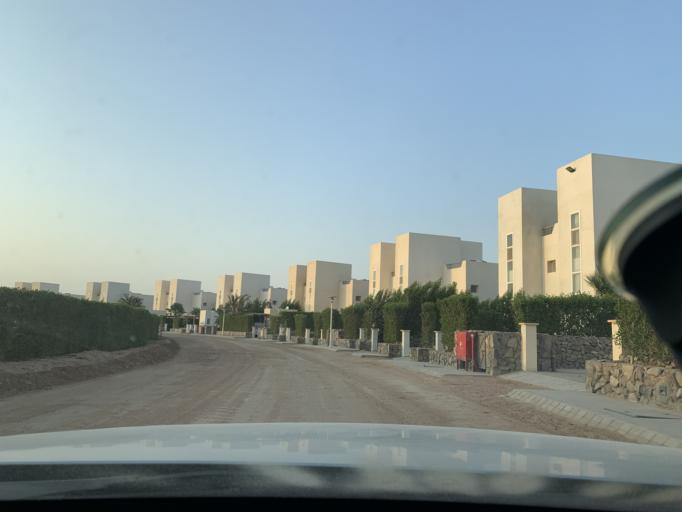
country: EG
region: Red Sea
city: El Gouna
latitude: 27.4088
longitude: 33.6675
